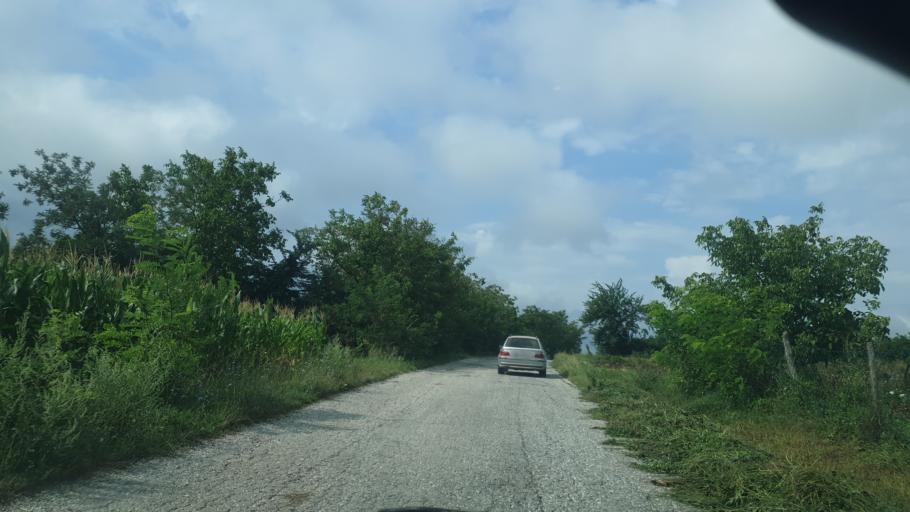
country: RS
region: Central Serbia
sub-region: Sumadijski Okrug
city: Kragujevac
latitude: 44.1065
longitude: 20.8023
